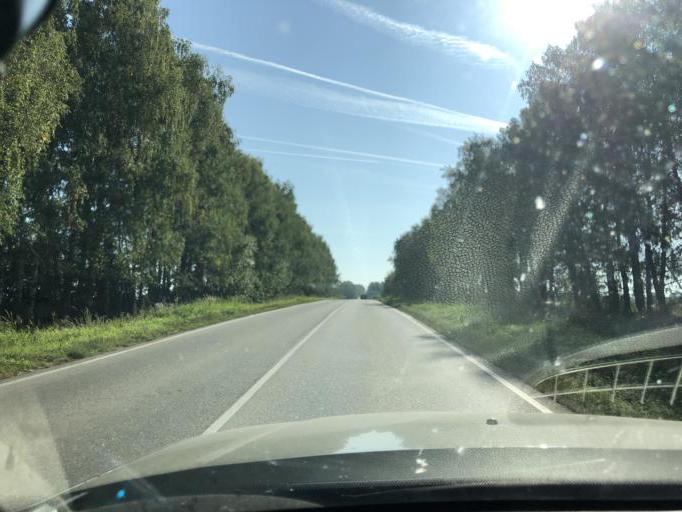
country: RU
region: Tula
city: Yasnogorsk
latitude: 54.4710
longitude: 37.5823
